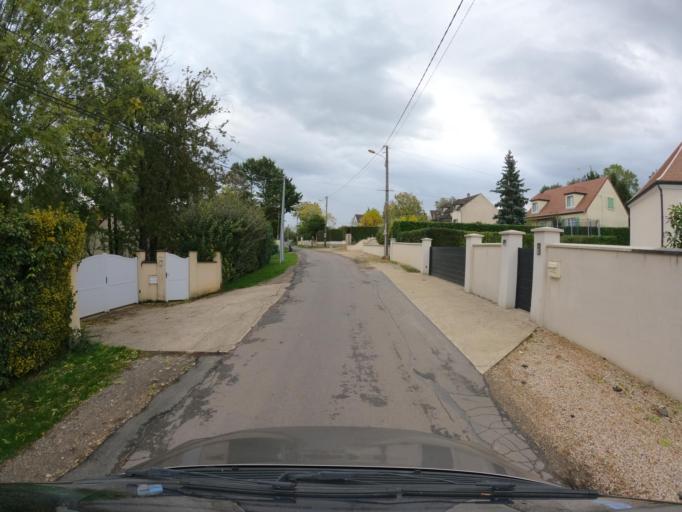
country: FR
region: Ile-de-France
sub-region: Departement de Seine-et-Marne
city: Saint-Germain-sur-Morin
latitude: 48.8727
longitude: 2.8452
